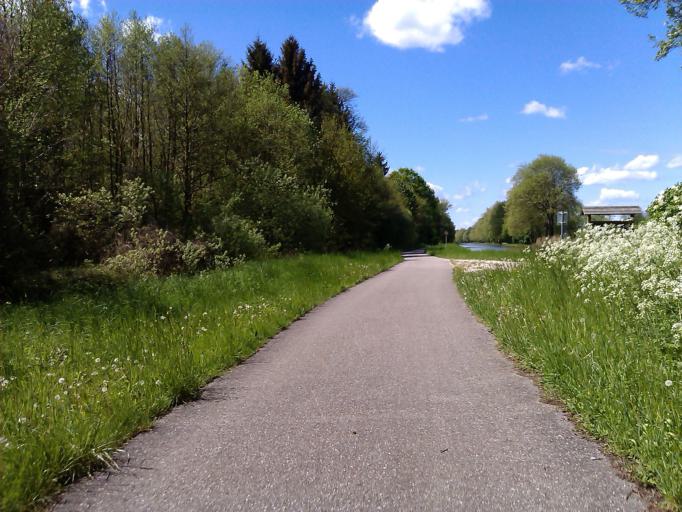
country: FR
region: Franche-Comte
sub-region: Territoire de Belfort
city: Montreux-Chateau
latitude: 47.6091
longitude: 7.0228
